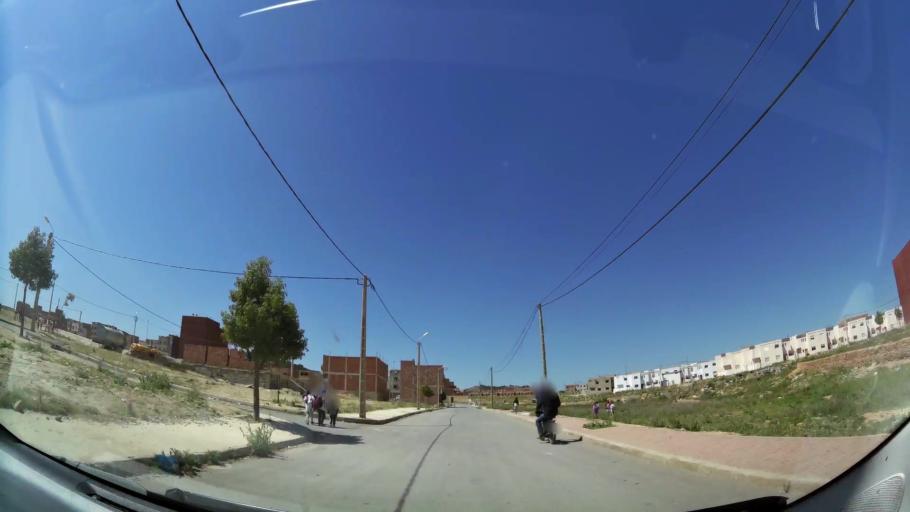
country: MA
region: Oriental
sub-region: Oujda-Angad
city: Oujda
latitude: 34.6526
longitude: -1.8743
